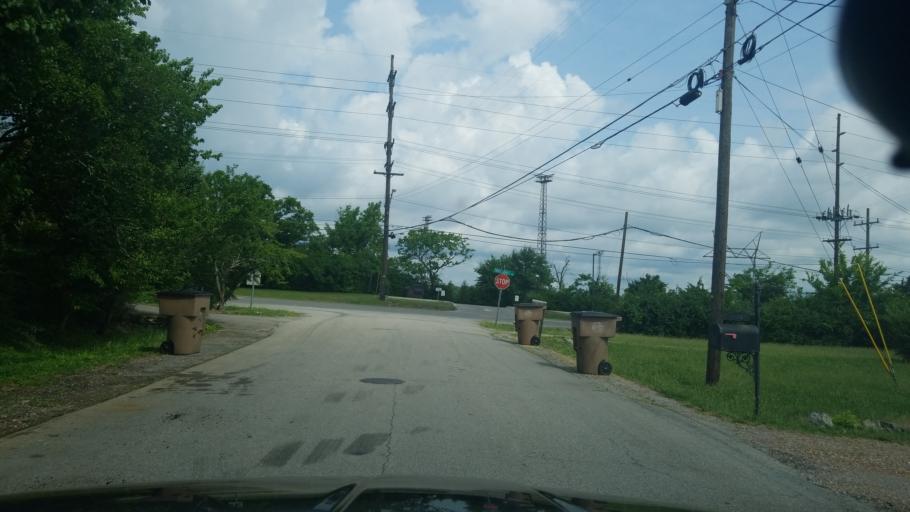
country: US
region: Tennessee
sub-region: Davidson County
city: Oak Hill
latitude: 36.0833
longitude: -86.7568
